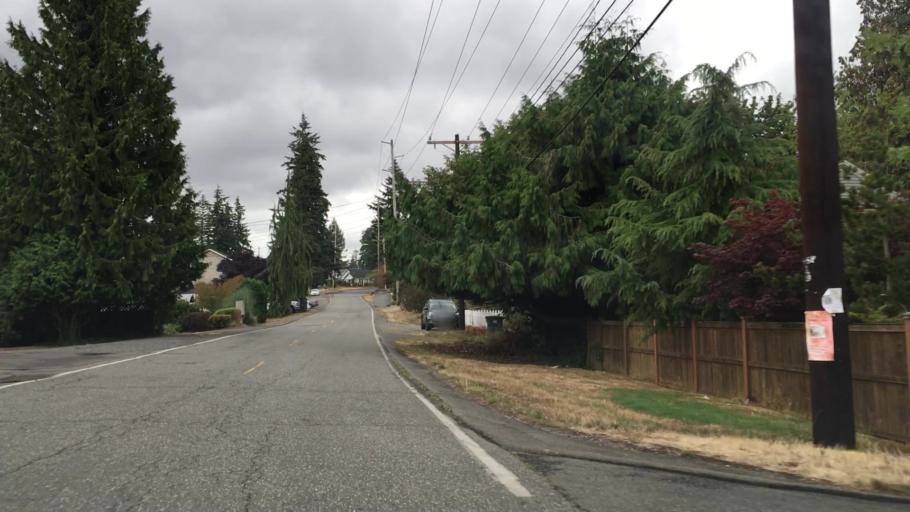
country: US
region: Washington
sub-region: Snohomish County
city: Everett
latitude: 47.9453
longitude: -122.2037
